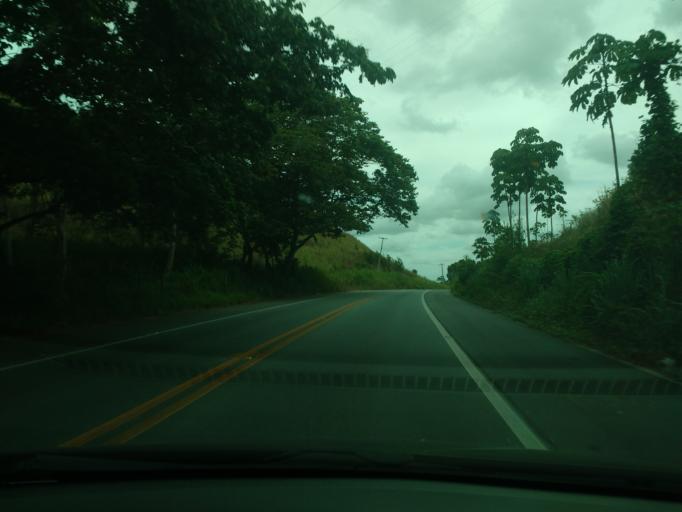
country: BR
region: Alagoas
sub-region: Murici
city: Murici
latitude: -9.2706
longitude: -35.9639
